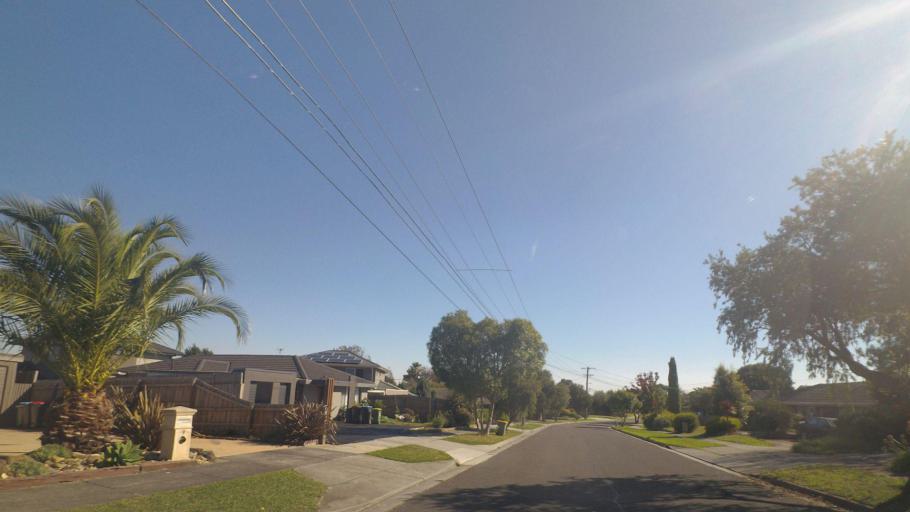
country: AU
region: Victoria
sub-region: Knox
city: Boronia
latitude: -37.8777
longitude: 145.2719
